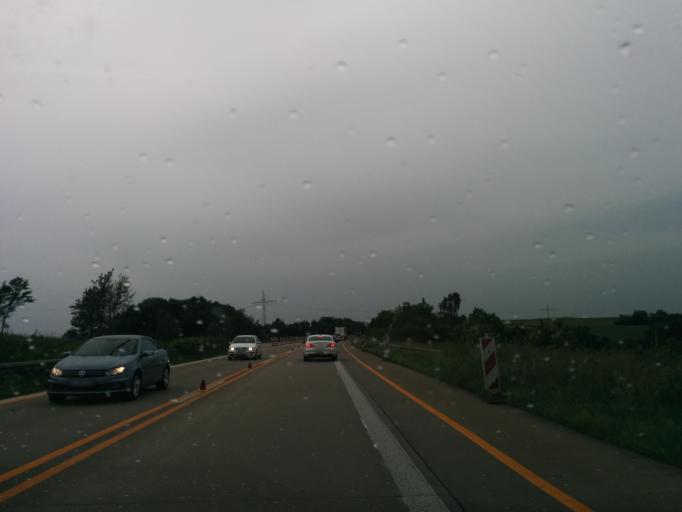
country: DE
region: Bavaria
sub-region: Regierungsbezirk Unterfranken
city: Marktbreit
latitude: 49.6568
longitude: 10.1342
